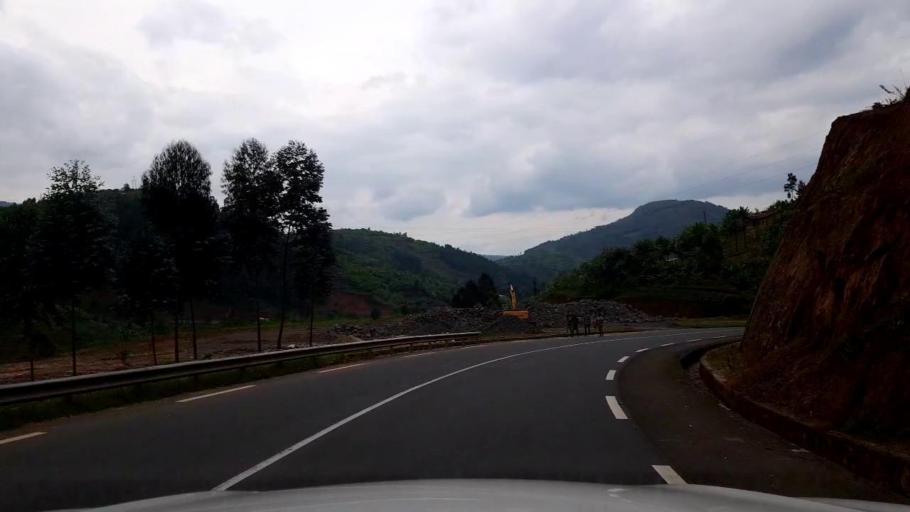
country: RW
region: Western Province
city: Kibuye
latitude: -1.9109
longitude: 29.3692
